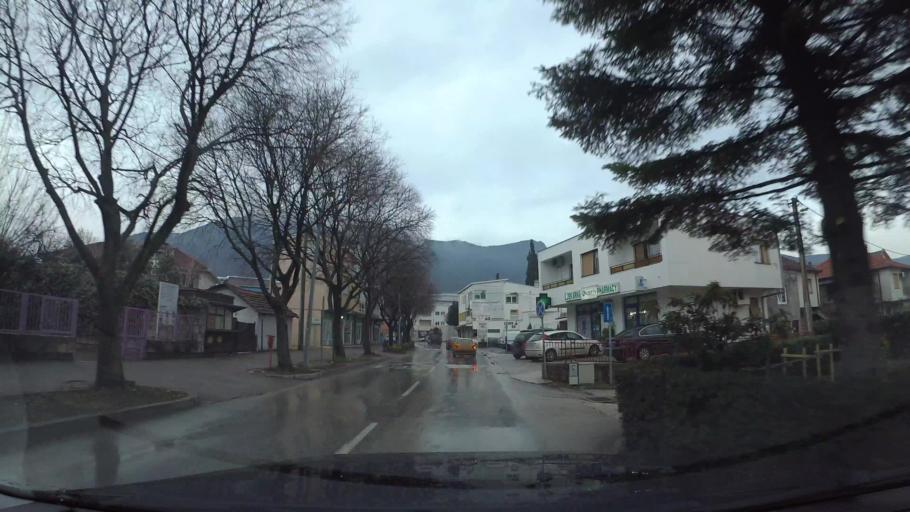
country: BA
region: Federation of Bosnia and Herzegovina
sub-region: Hercegovacko-Bosanski Kanton
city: Mostar
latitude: 43.3543
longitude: 17.8001
